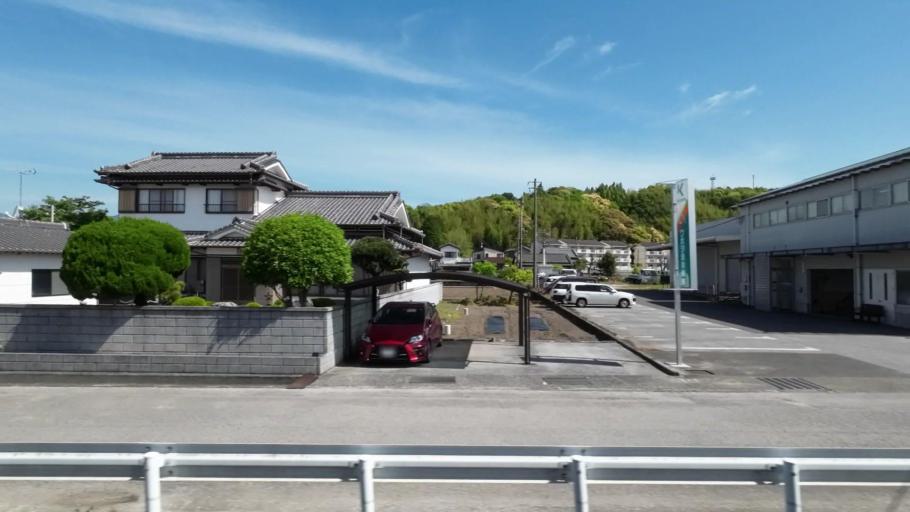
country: JP
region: Kochi
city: Kochi-shi
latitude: 33.5783
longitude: 133.6336
